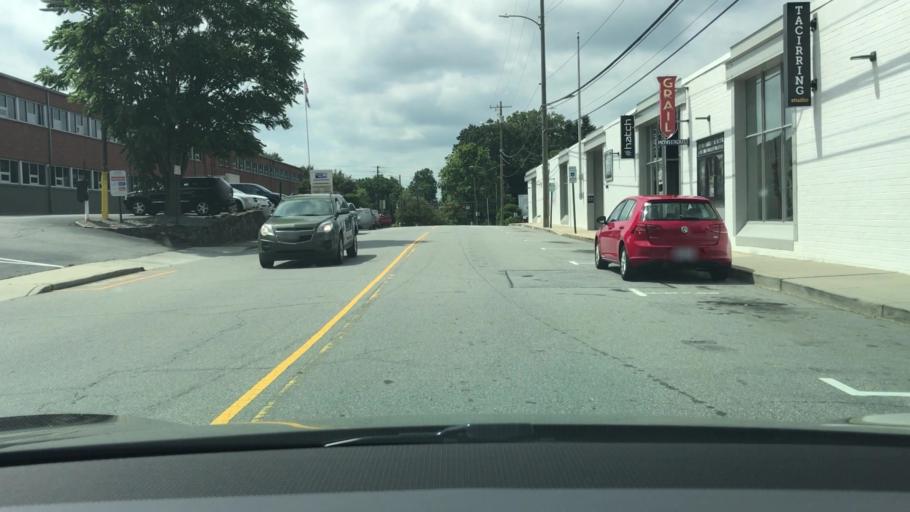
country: US
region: North Carolina
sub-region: Buncombe County
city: Asheville
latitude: 35.5925
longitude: -82.5588
